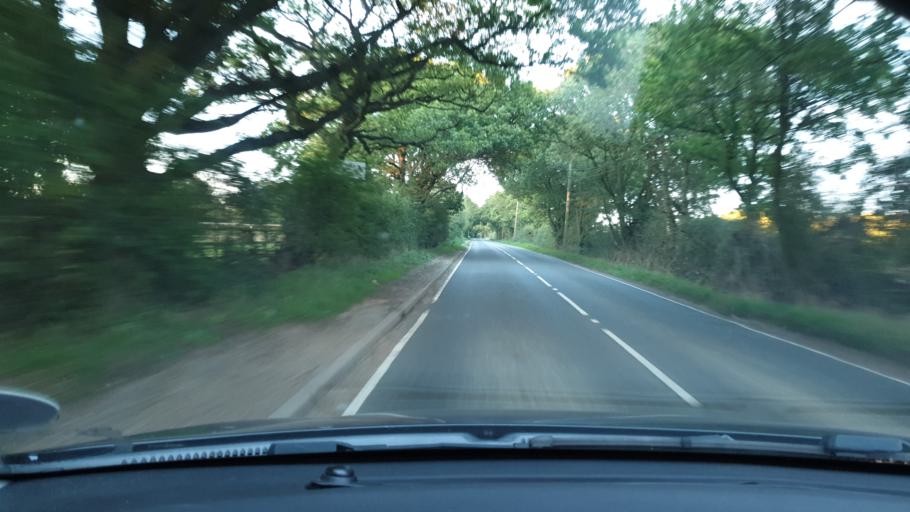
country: GB
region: England
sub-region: Essex
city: Rowhedge
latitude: 51.8988
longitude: 0.9571
